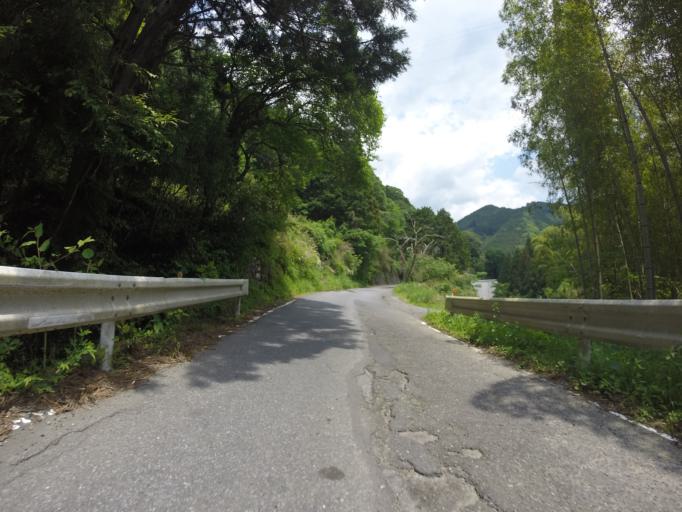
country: JP
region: Shizuoka
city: Shizuoka-shi
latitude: 35.1237
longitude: 138.2974
